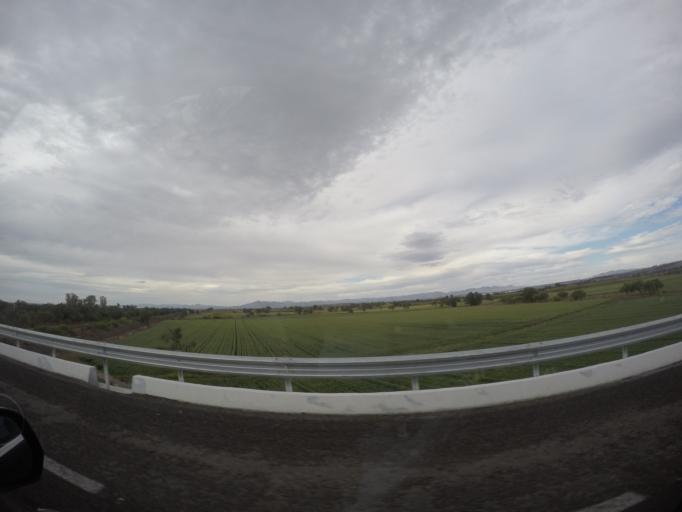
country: MX
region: Guanajuato
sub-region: Irapuato
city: Serrano
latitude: 20.7830
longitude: -101.4135
